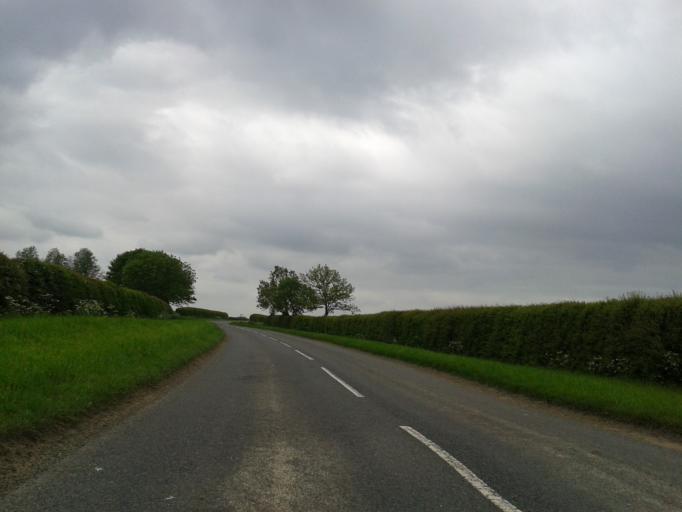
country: GB
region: England
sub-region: Northamptonshire
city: Corby
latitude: 52.5180
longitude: -0.7281
